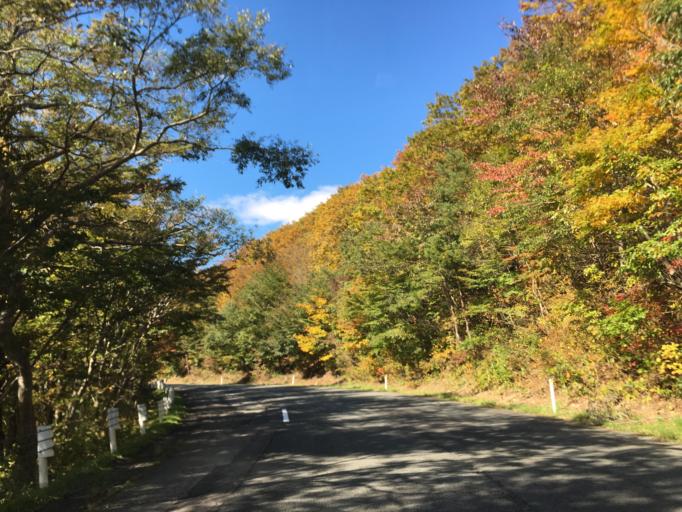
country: JP
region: Fukushima
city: Inawashiro
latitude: 37.5842
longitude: 140.2452
